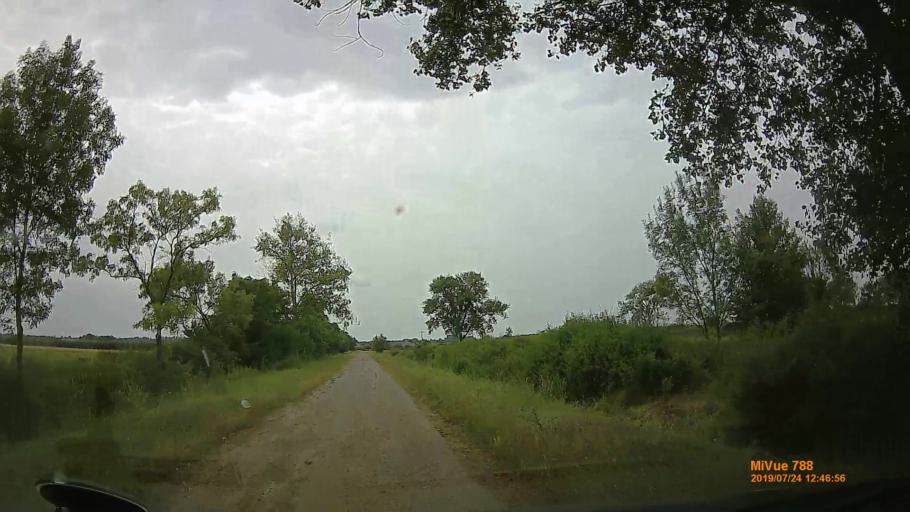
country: HU
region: Szabolcs-Szatmar-Bereg
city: Aranyosapati
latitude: 48.1959
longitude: 22.3198
